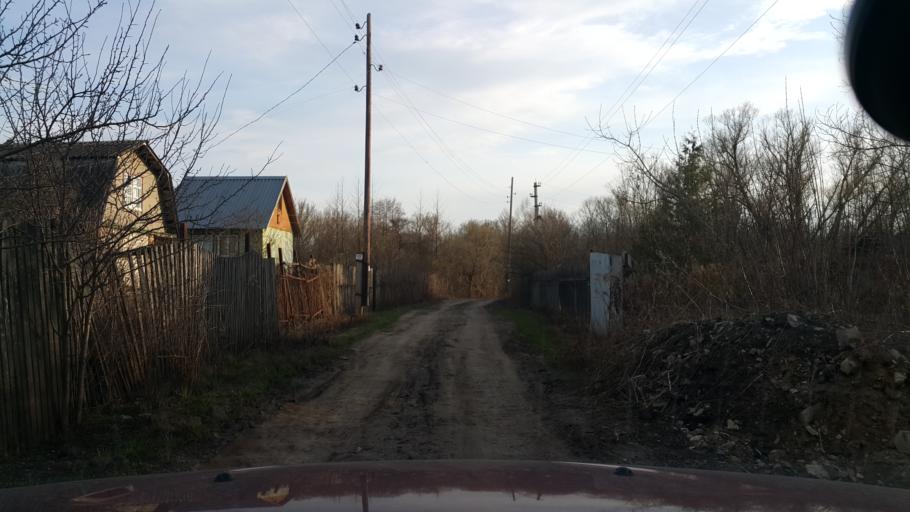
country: RU
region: Tambov
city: Kotovsk
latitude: 52.5912
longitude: 41.4661
